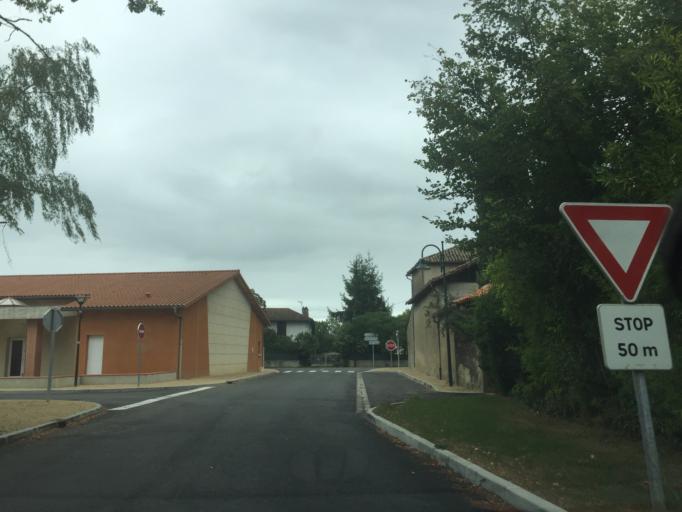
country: FR
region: Midi-Pyrenees
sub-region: Departement des Hautes-Pyrenees
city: Orleix
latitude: 43.3037
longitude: 0.2300
